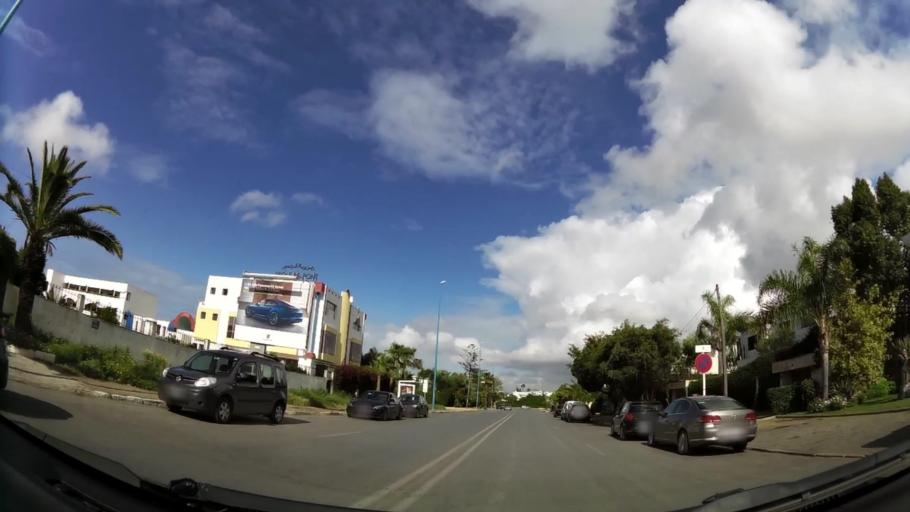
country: MA
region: Grand Casablanca
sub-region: Casablanca
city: Casablanca
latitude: 33.5479
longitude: -7.6281
